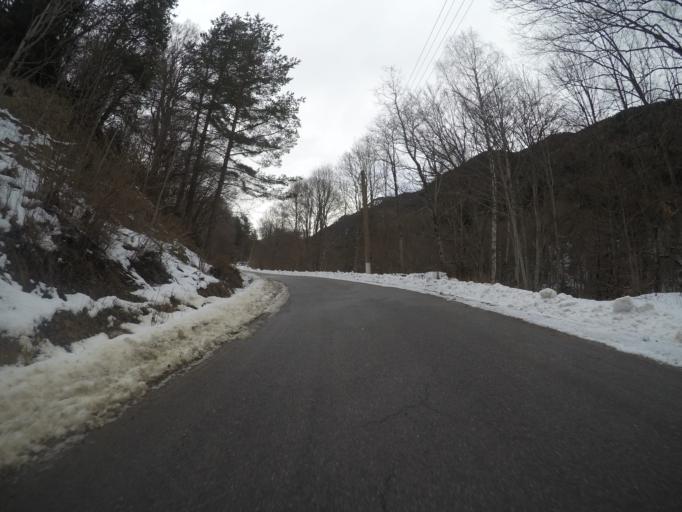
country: BG
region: Kyustendil
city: Sapareva Banya
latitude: 42.1411
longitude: 23.3540
